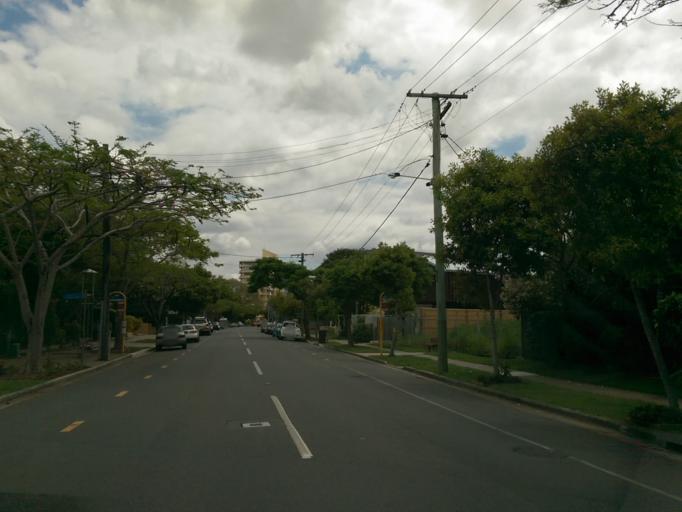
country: AU
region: Queensland
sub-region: Brisbane
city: Woolloongabba
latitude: -27.4739
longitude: 153.0475
